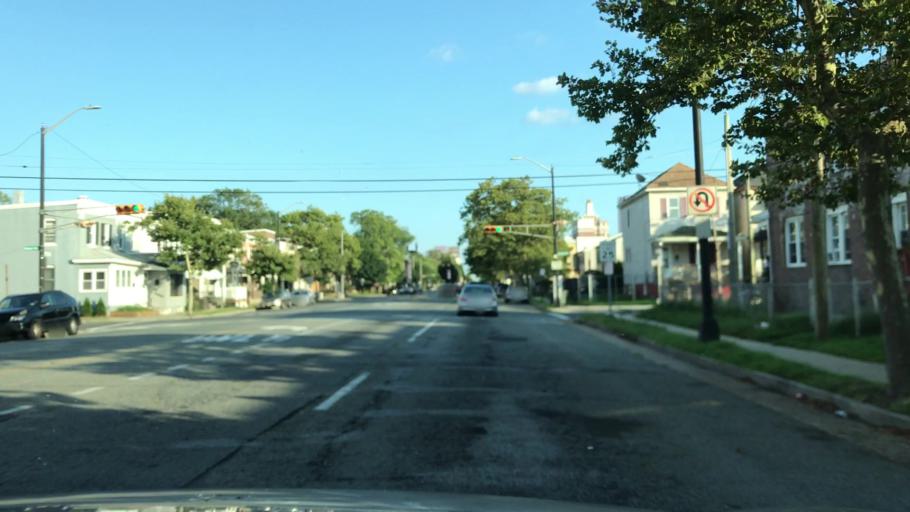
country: US
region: New Jersey
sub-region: Atlantic County
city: Atlantic City
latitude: 39.3670
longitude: -74.4363
